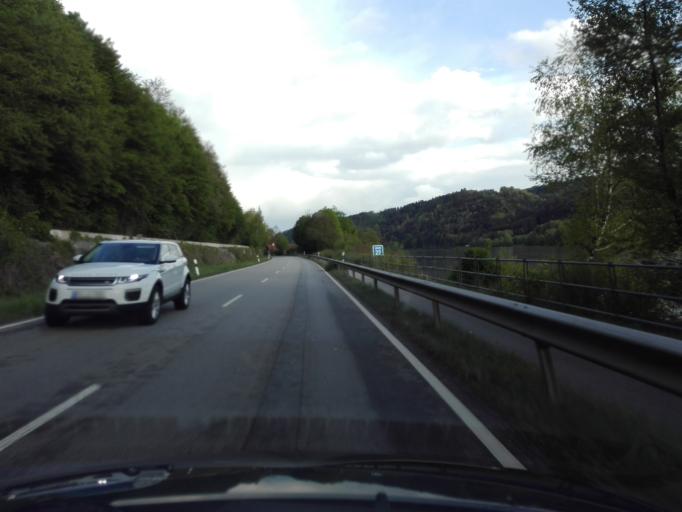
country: DE
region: Bavaria
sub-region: Lower Bavaria
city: Obernzell
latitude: 48.5637
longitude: 13.6128
